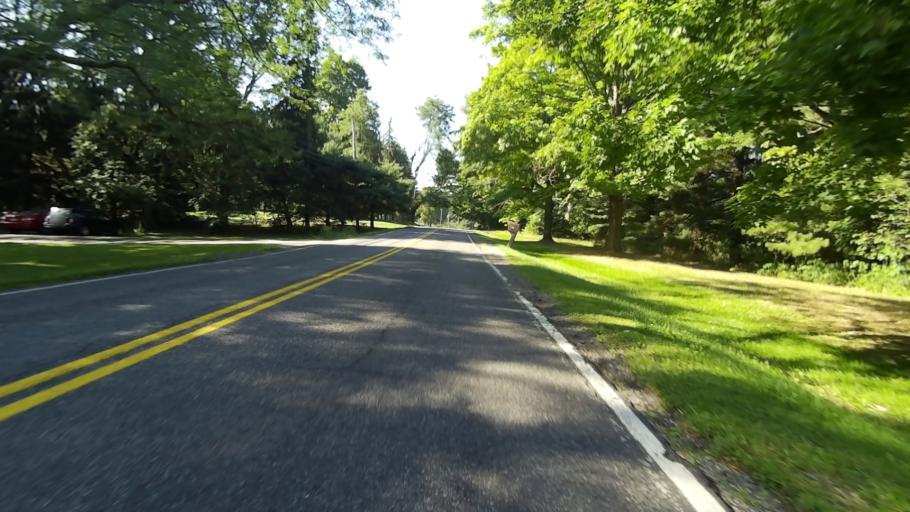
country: US
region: Ohio
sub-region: Portage County
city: Streetsboro
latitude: 41.1968
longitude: -81.3289
